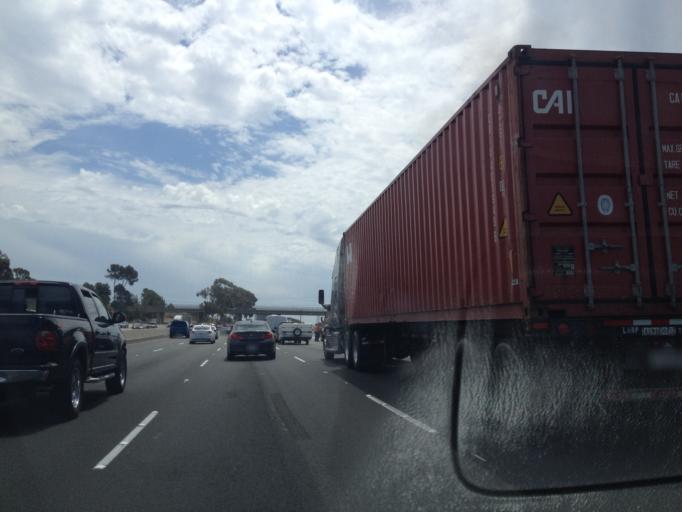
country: US
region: California
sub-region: Orange County
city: Dana Point
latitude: 33.4676
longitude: -117.6710
